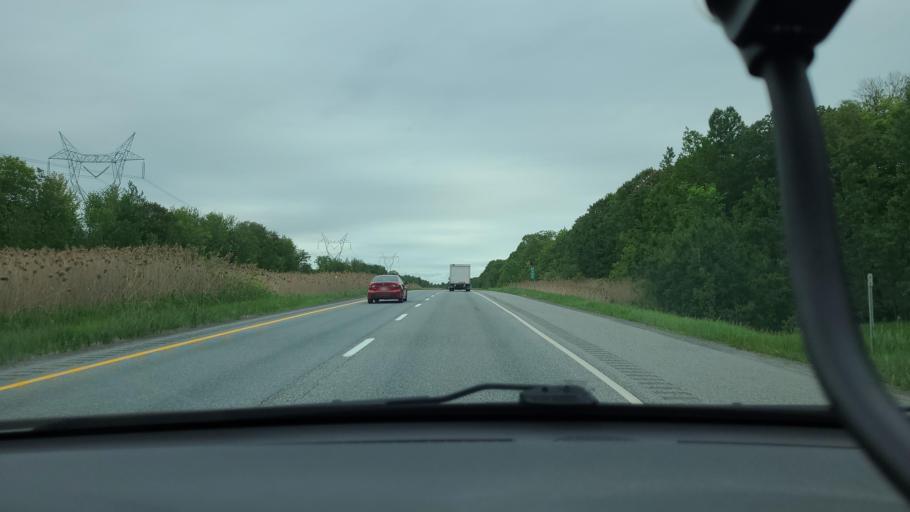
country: CA
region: Quebec
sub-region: Lanaudiere
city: Mascouche
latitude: 45.7992
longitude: -73.5856
